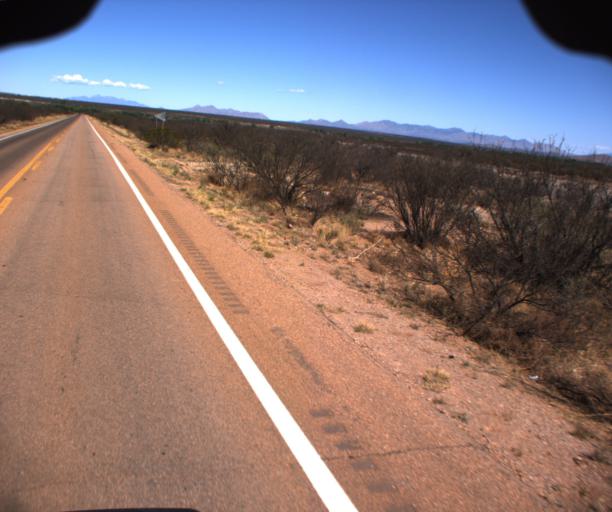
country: US
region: Arizona
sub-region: Cochise County
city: Sierra Vista Southeast
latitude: 31.5523
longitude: -110.1206
